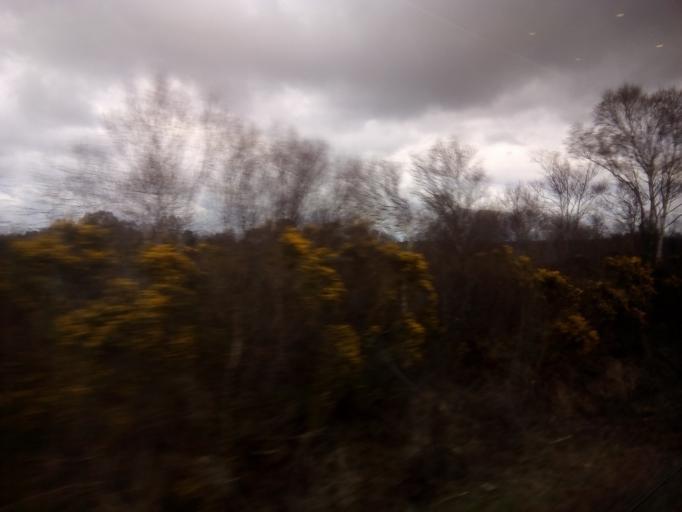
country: IE
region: Leinster
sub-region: An Longfort
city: Longford
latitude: 53.8015
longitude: -7.8558
